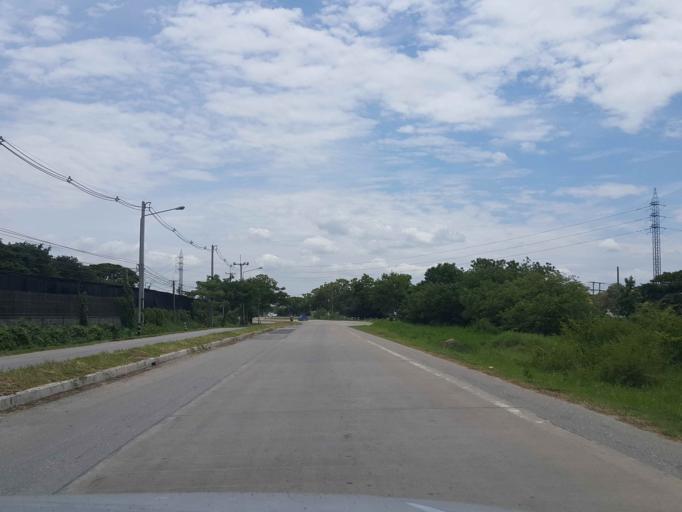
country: TH
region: Chiang Mai
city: Saraphi
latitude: 18.7343
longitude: 99.0394
